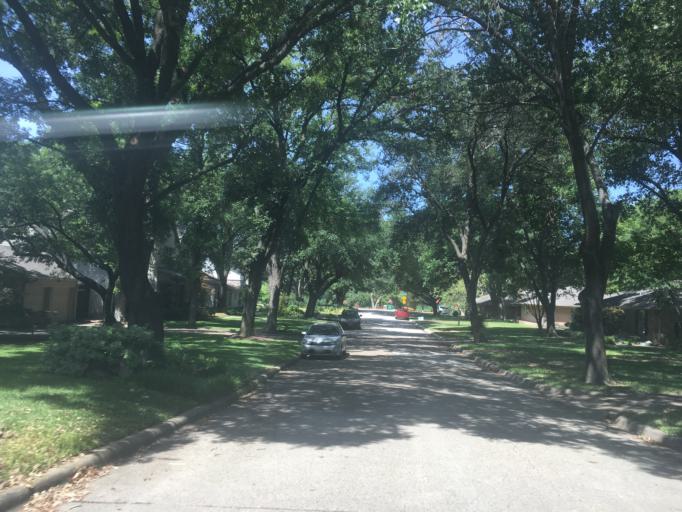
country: US
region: Texas
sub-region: Dallas County
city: University Park
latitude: 32.8730
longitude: -96.7362
